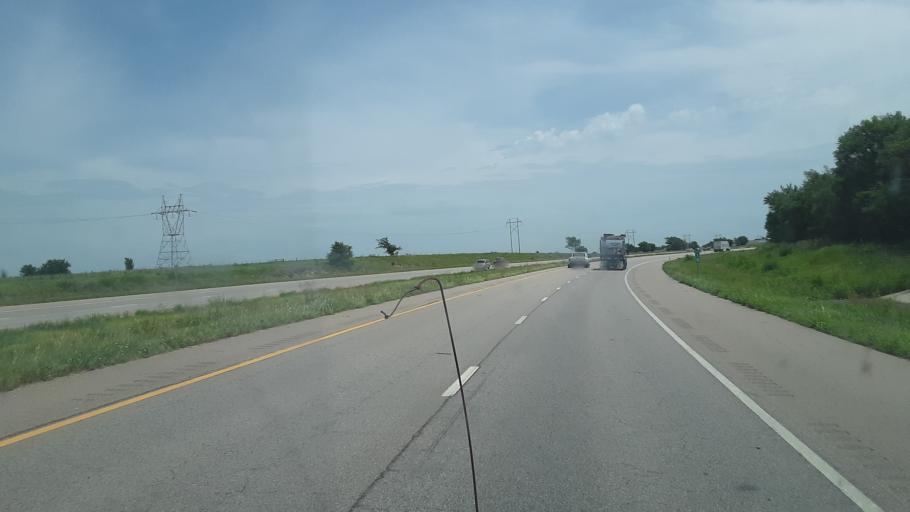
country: US
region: Kansas
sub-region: Butler County
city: Towanda
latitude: 37.8045
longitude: -96.9999
